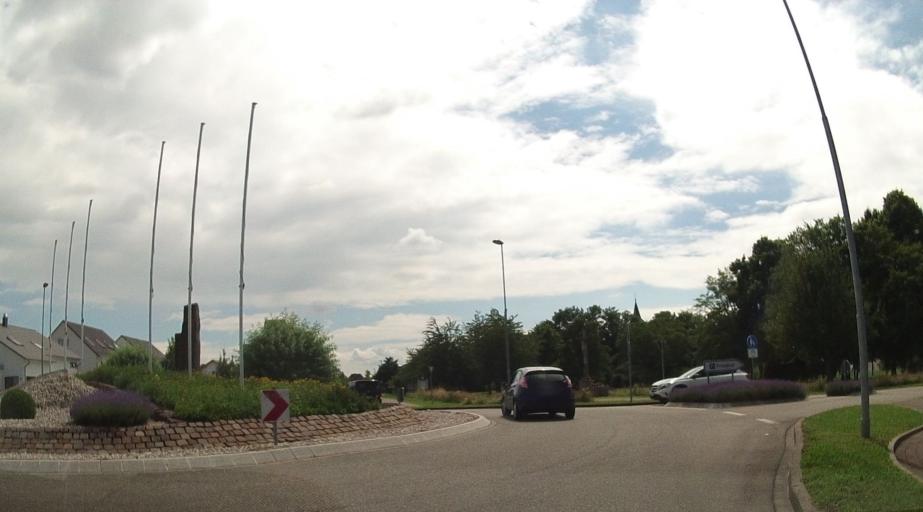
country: DE
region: Baden-Wuerttemberg
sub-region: Karlsruhe Region
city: Bietigheim
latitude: 48.9156
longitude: 8.2563
